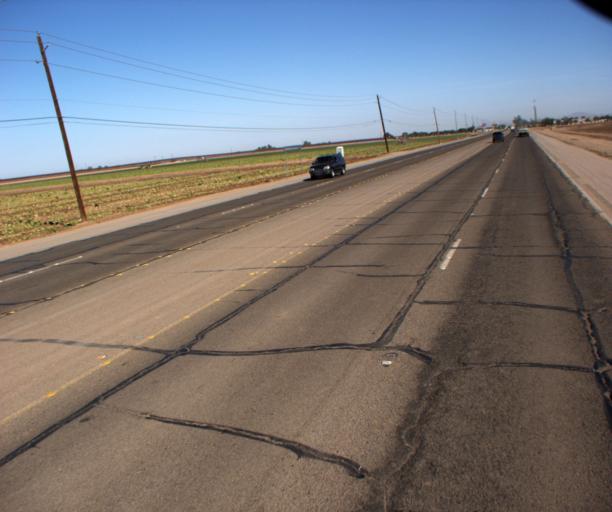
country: US
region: Arizona
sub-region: Yuma County
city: San Luis
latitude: 32.5386
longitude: -114.7868
